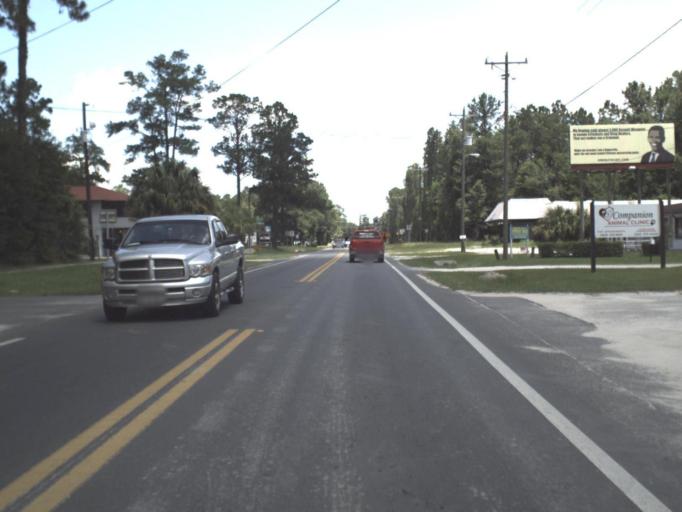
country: US
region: Florida
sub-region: Clay County
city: Keystone Heights
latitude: 29.7113
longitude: -82.0442
